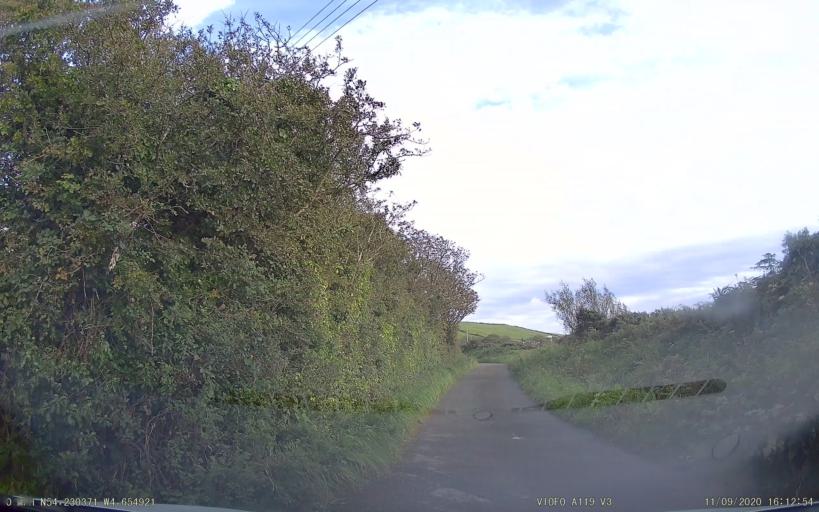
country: IM
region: Castletown
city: Castletown
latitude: 54.2304
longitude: -4.6549
